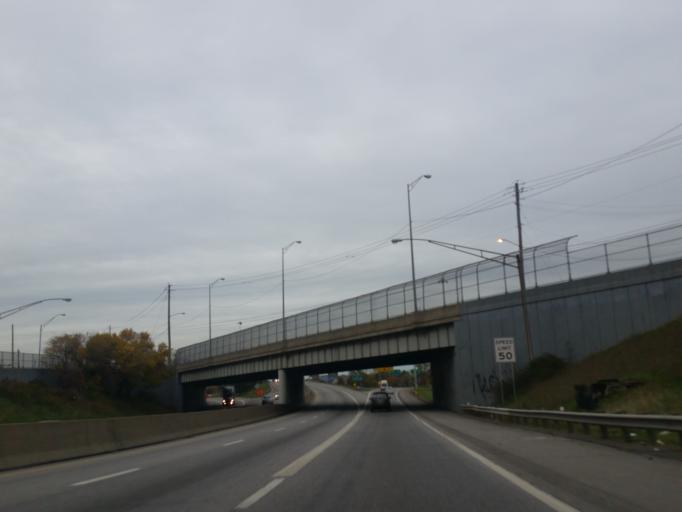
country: US
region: Ohio
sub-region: Cuyahoga County
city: Newburgh Heights
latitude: 41.4750
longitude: -81.6602
